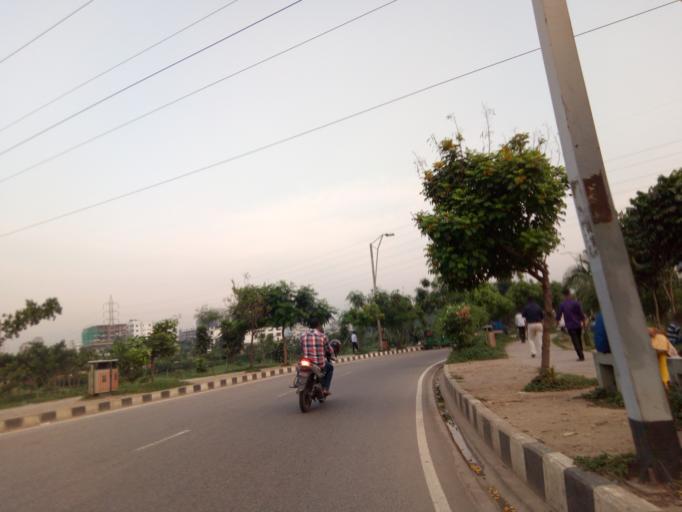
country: BD
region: Dhaka
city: Paltan
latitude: 23.7702
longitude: 90.4229
